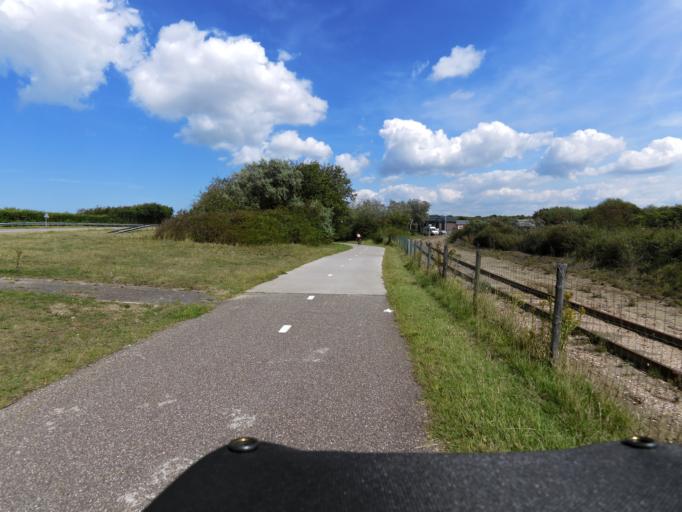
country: NL
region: Zeeland
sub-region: Schouwen-Duiveland
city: Scharendijke
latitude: 51.7834
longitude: 3.8706
